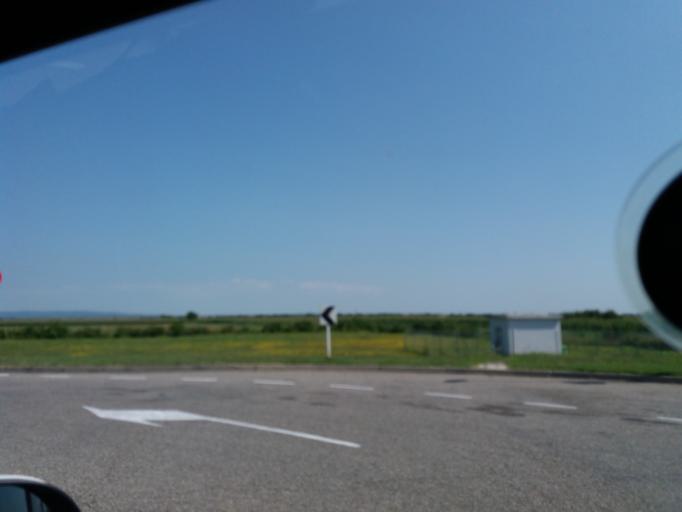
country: RS
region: Autonomna Pokrajina Vojvodina
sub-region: Sremski Okrug
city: Pecinci
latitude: 44.9345
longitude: 19.9155
